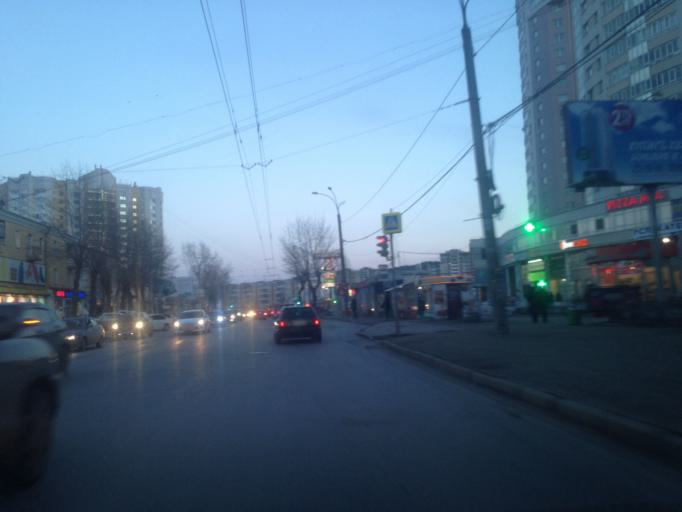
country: RU
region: Sverdlovsk
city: Yekaterinburg
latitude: 56.8009
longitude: 60.6298
